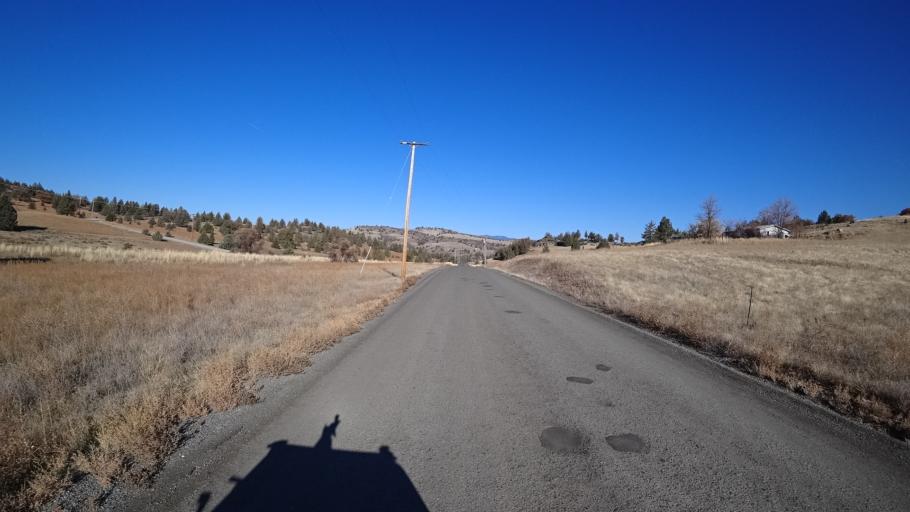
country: US
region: California
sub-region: Siskiyou County
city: Montague
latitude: 41.8824
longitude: -122.4252
